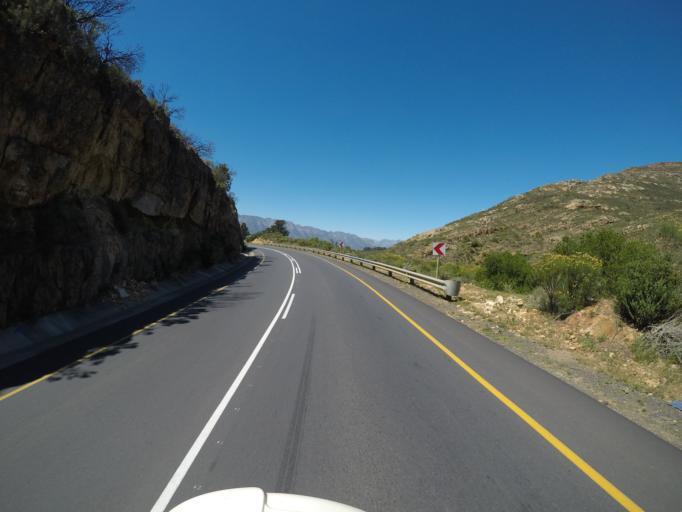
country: ZA
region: Western Cape
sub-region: Cape Winelands District Municipality
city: Ceres
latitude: -33.3178
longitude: 19.0890
